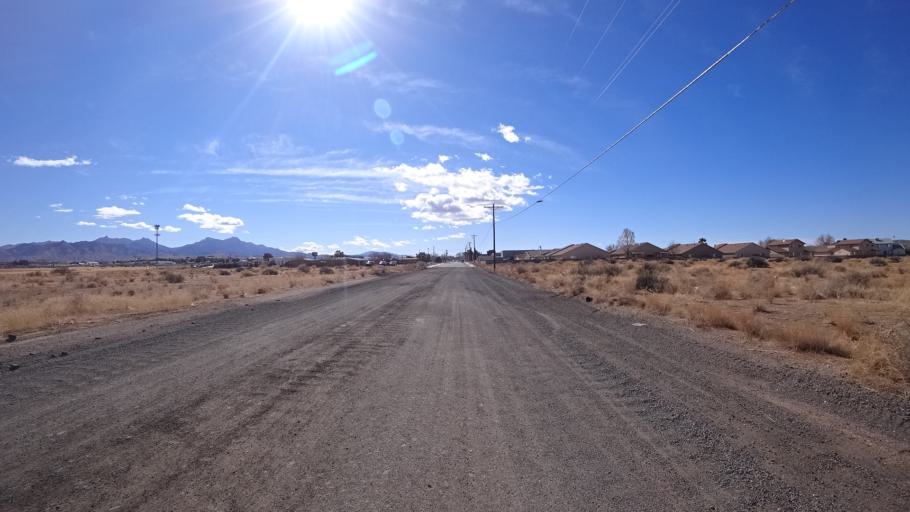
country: US
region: Arizona
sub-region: Mohave County
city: New Kingman-Butler
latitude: 35.2222
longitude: -114.0204
